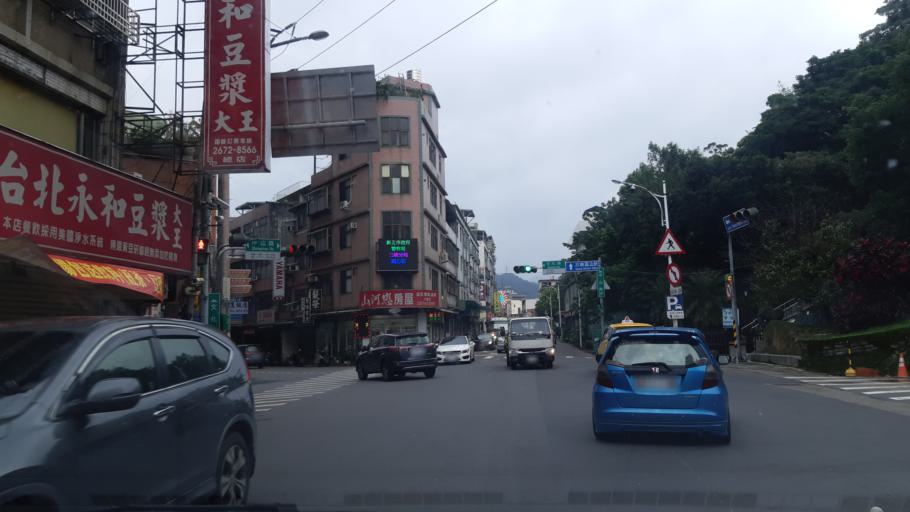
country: TW
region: Taiwan
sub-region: Taoyuan
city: Taoyuan
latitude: 24.9358
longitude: 121.3657
